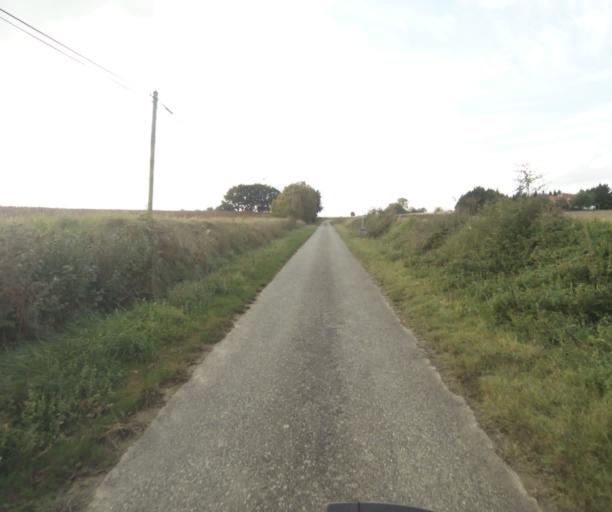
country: FR
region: Midi-Pyrenees
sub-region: Departement du Tarn-et-Garonne
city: Beaumont-de-Lomagne
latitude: 43.8220
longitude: 1.0863
